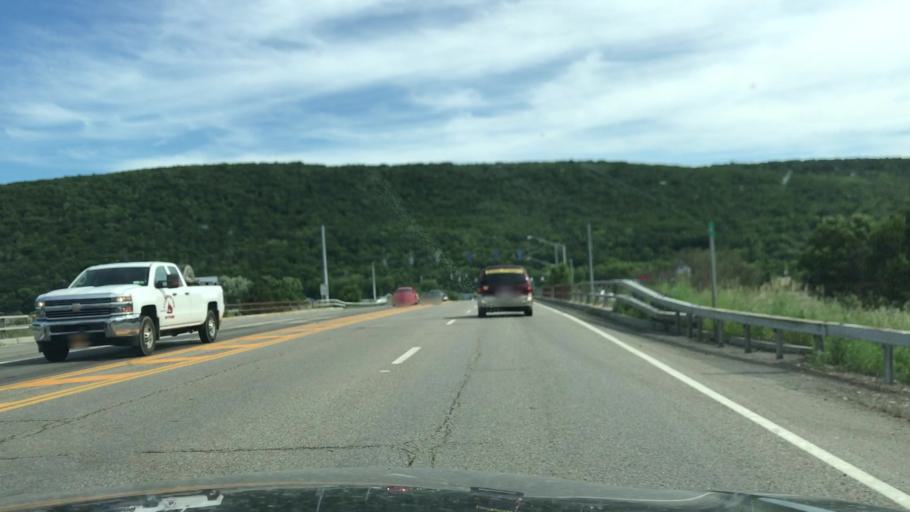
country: US
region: New York
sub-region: Chemung County
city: Horseheads
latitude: 42.1573
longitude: -76.8779
